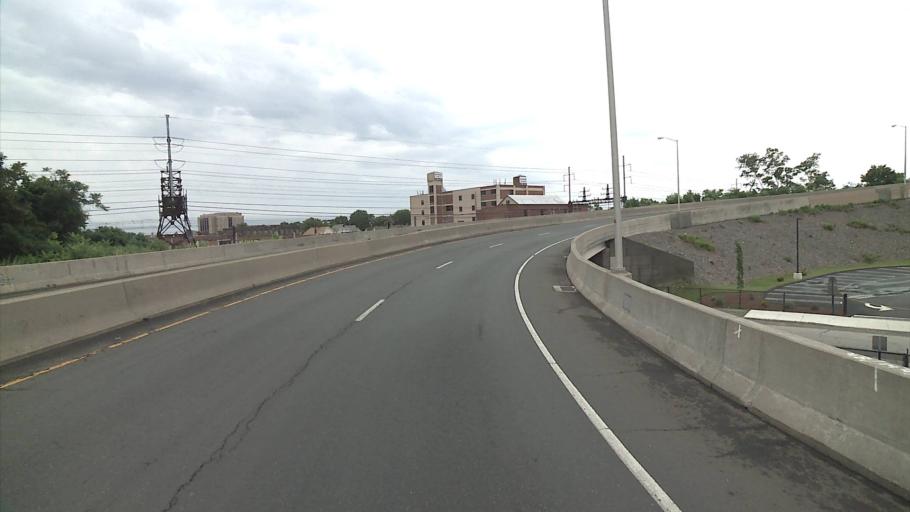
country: US
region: Connecticut
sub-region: Fairfield County
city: Bridgeport
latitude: 41.1705
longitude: -73.1907
